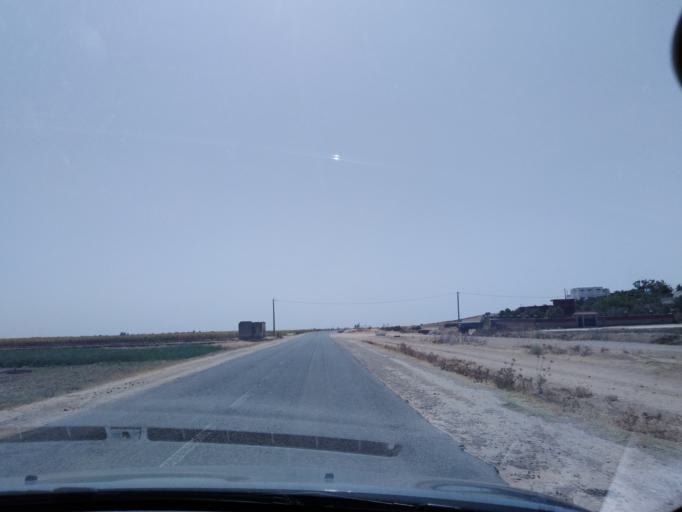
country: MA
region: Doukkala-Abda
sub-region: Safi
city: Safi
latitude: 32.4757
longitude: -8.8726
